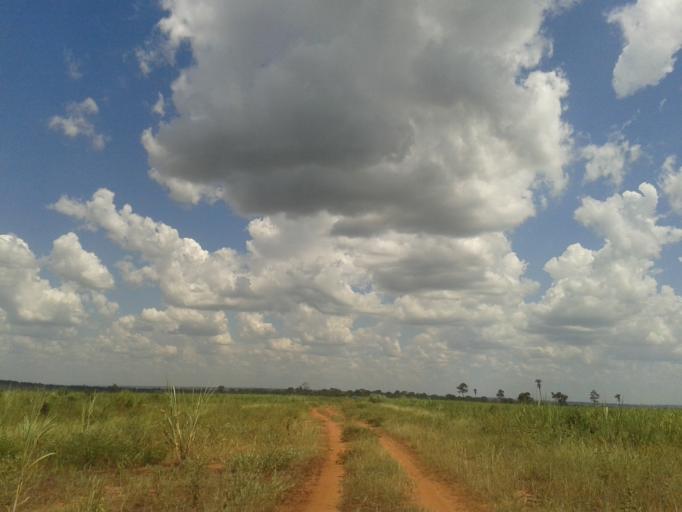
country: BR
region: Minas Gerais
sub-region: Santa Vitoria
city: Santa Vitoria
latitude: -19.1768
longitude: -50.4503
